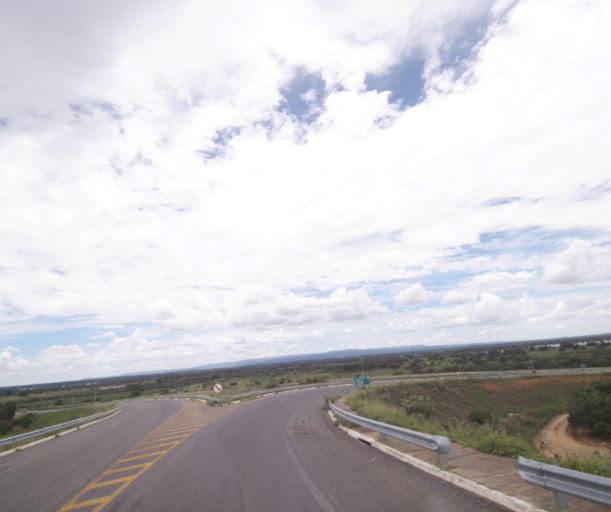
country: BR
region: Bahia
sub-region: Carinhanha
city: Carinhanha
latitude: -14.3269
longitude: -43.7654
